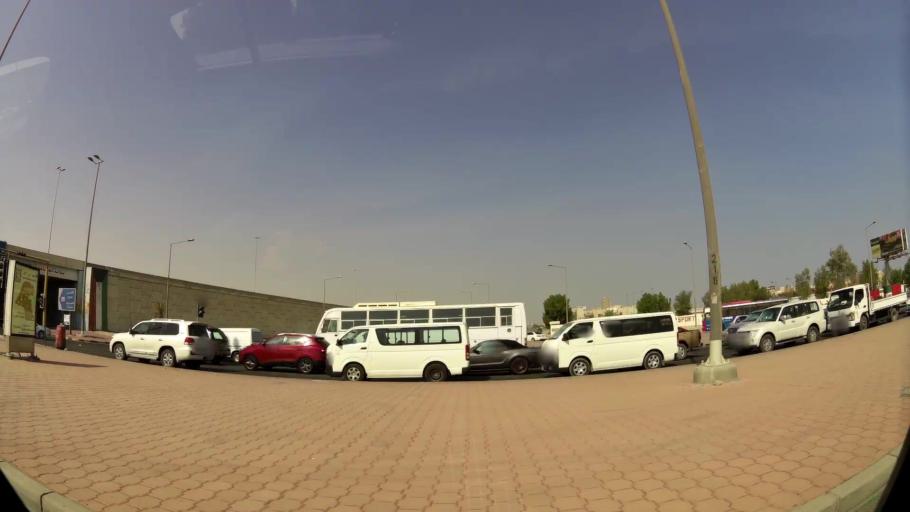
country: KW
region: Al Ahmadi
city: Al Fahahil
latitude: 29.0907
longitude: 48.1167
